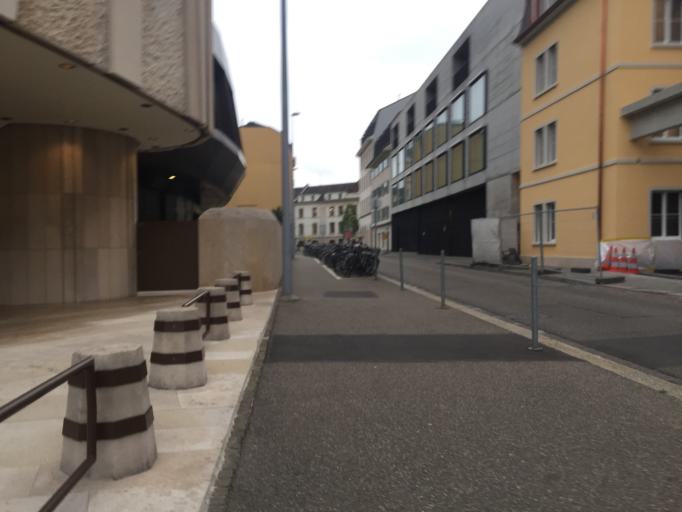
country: CH
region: Basel-City
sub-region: Basel-Stadt
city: Basel
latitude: 47.5483
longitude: 7.5912
